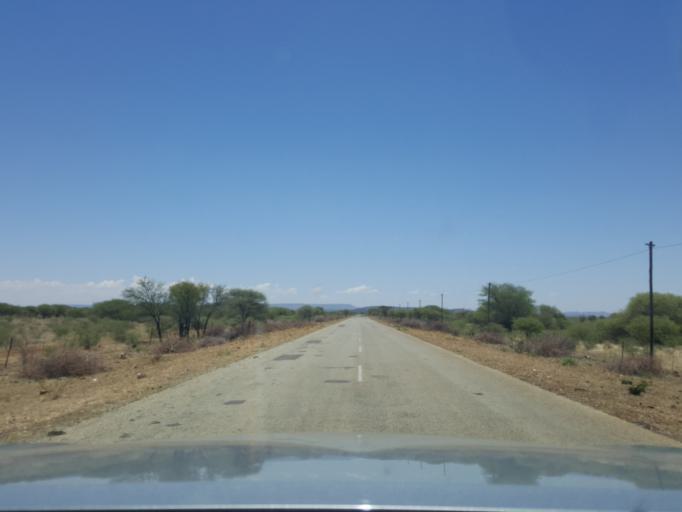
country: BW
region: South East
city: Ramotswa
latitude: -25.0340
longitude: 25.9274
